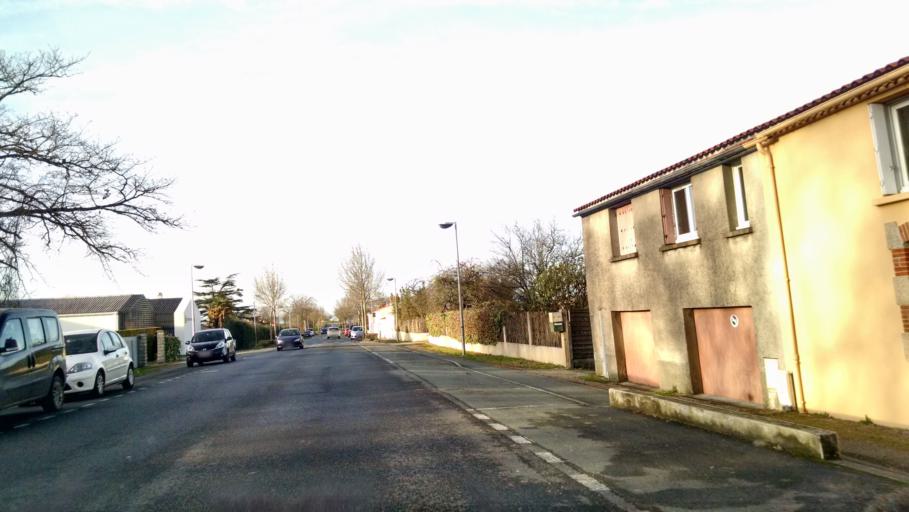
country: FR
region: Pays de la Loire
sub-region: Departement de la Vendee
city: Saint-Hilaire-de-Loulay
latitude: 47.0049
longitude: -1.3341
